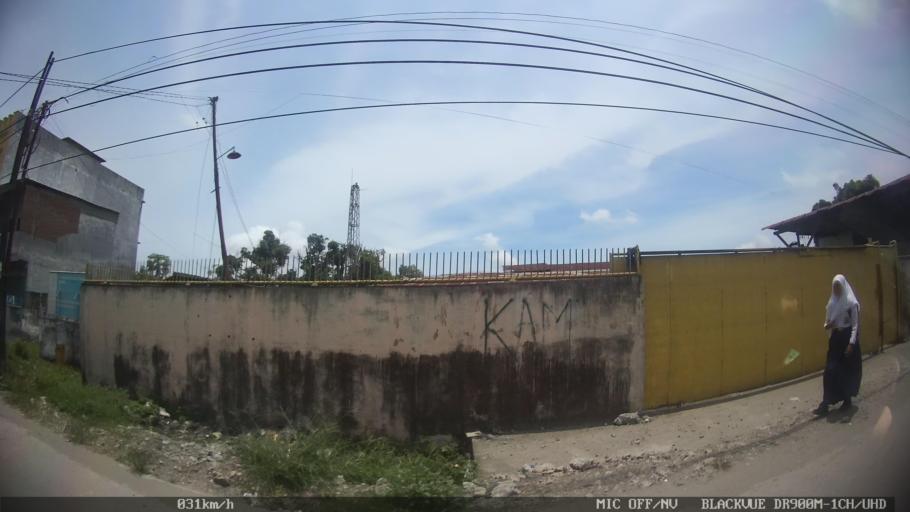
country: ID
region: North Sumatra
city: Labuhan Deli
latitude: 3.7194
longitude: 98.6805
